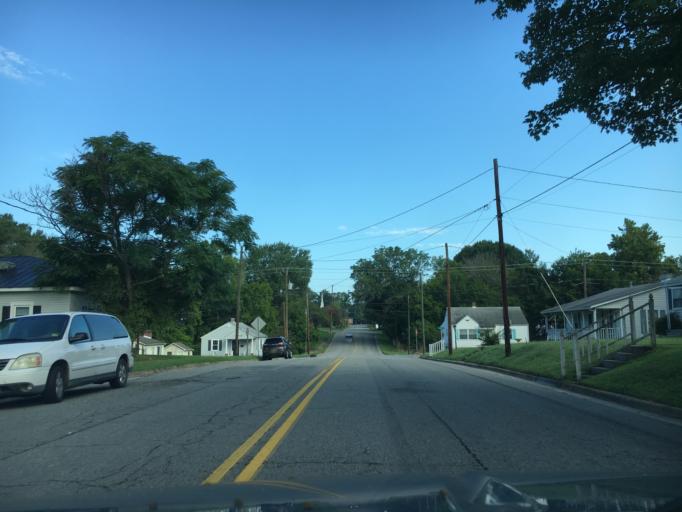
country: US
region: Virginia
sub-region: Halifax County
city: South Boston
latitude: 36.7016
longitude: -78.9098
